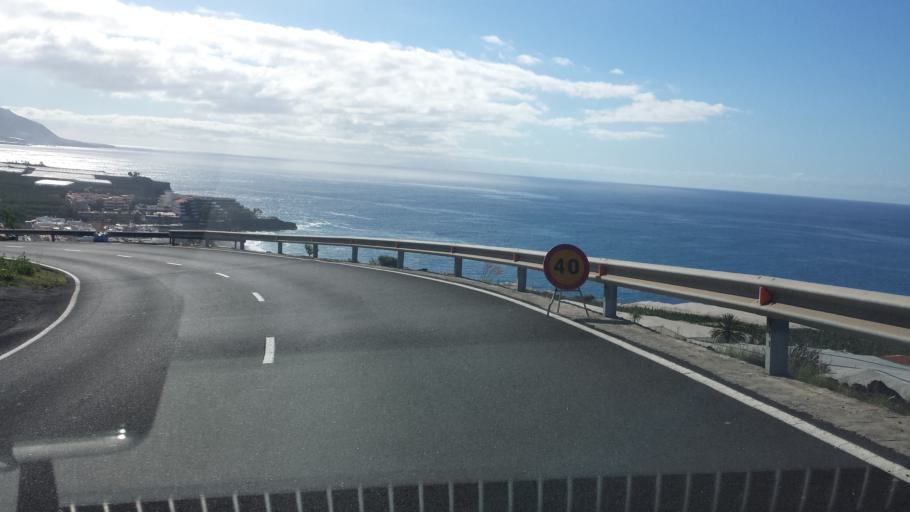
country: ES
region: Canary Islands
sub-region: Provincia de Santa Cruz de Tenerife
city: Tazacorte
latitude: 28.5918
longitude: -17.9116
